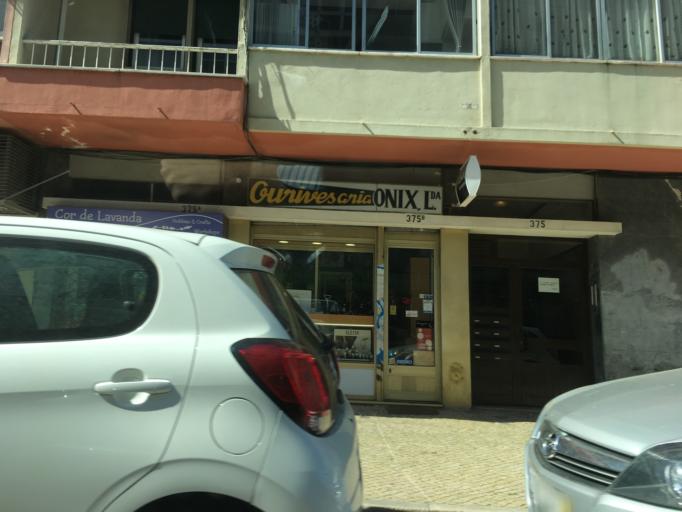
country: PT
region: Lisbon
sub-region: Odivelas
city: Pontinha
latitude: 38.7448
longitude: -9.1802
